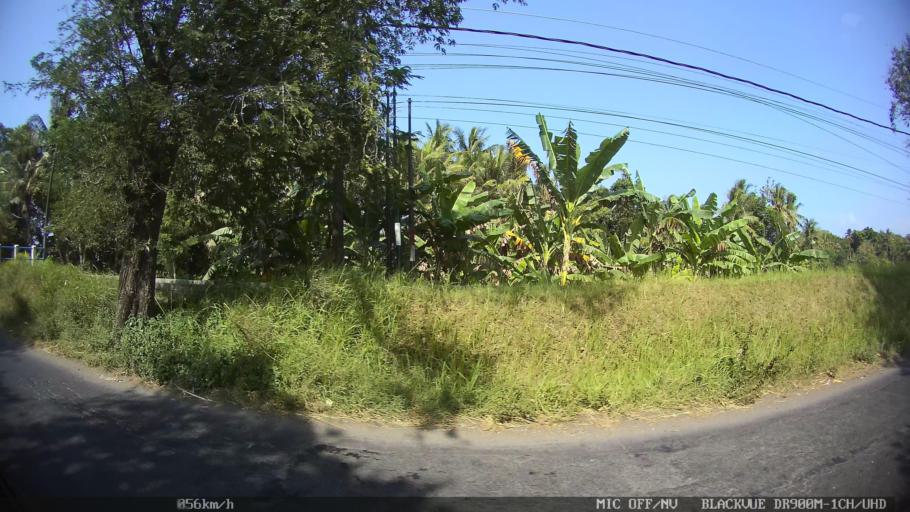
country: ID
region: Daerah Istimewa Yogyakarta
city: Srandakan
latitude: -7.9245
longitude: 110.1872
